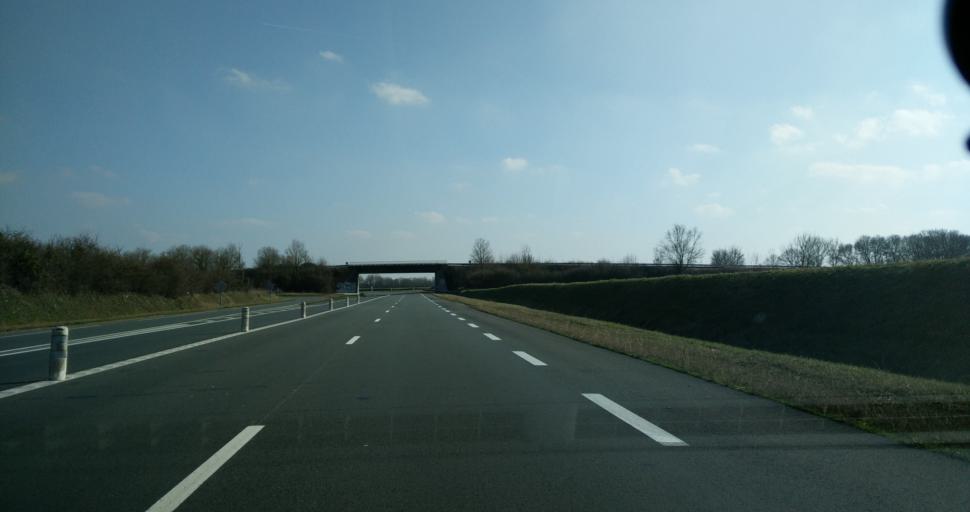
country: FR
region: Poitou-Charentes
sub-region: Departement des Deux-Sevres
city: Mauze-sur-le-Mignon
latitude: 46.1901
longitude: -0.6810
